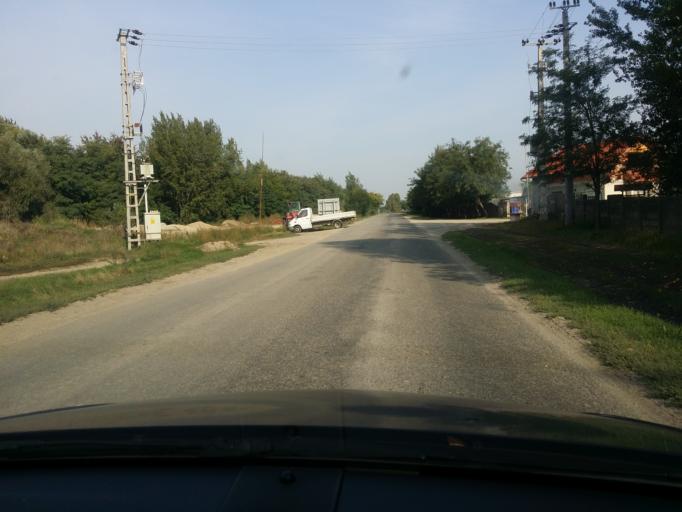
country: HU
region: Pest
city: Taksony
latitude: 47.3120
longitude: 19.0794
